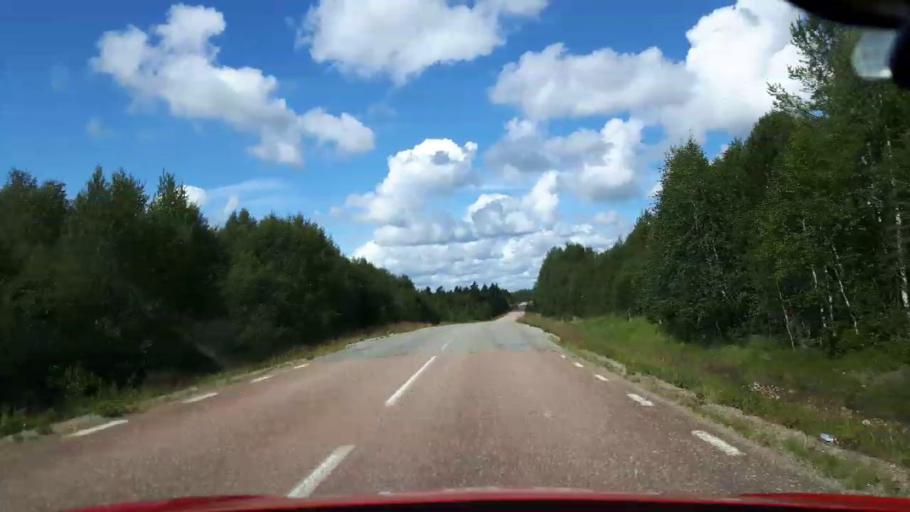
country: SE
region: Dalarna
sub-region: Alvdalens Kommun
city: AElvdalen
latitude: 61.8001
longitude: 13.6691
